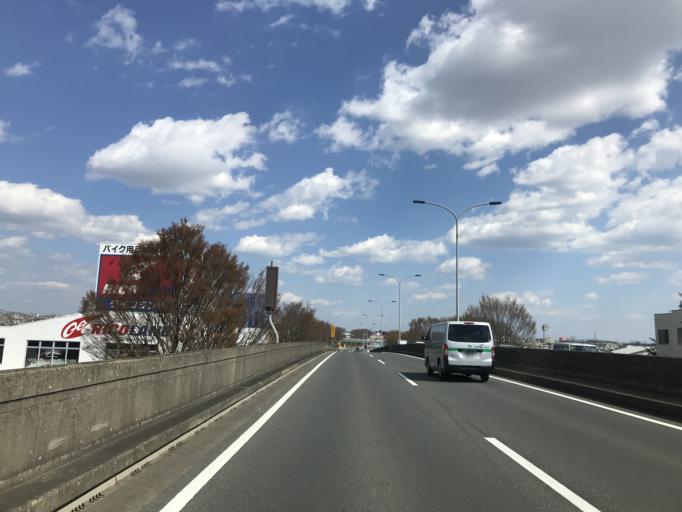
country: JP
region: Ibaraki
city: Mito-shi
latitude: 36.3475
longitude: 140.4644
